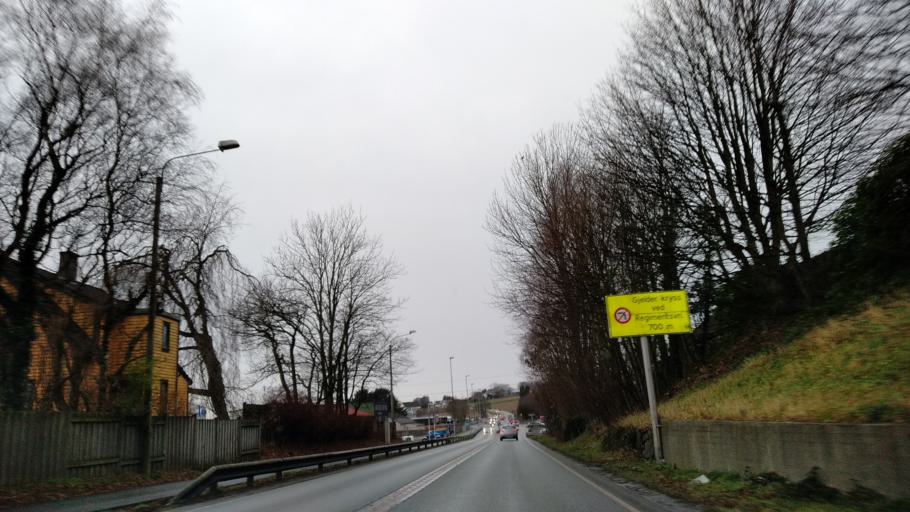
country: NO
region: Rogaland
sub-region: Randaberg
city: Randaberg
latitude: 58.9517
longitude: 5.6591
